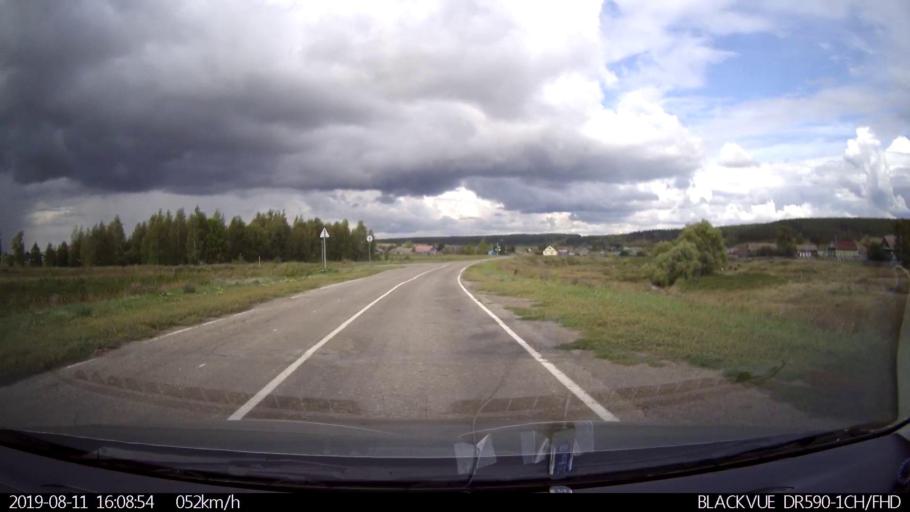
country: RU
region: Ulyanovsk
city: Ignatovka
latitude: 53.9882
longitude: 47.6496
